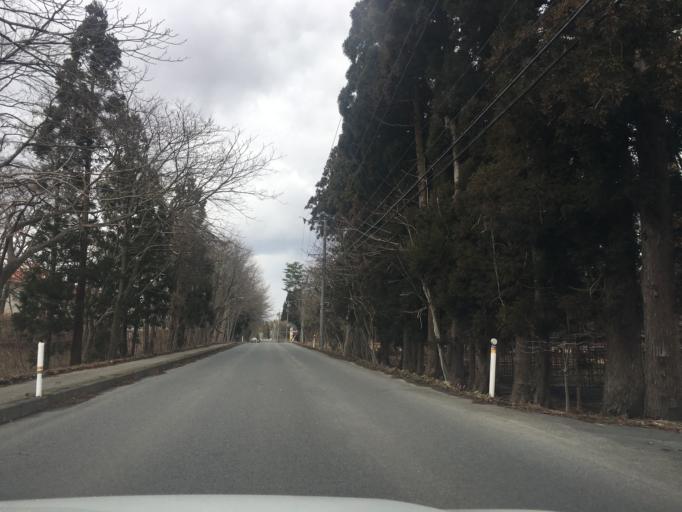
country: JP
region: Akita
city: Takanosu
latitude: 40.1808
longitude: 140.3445
